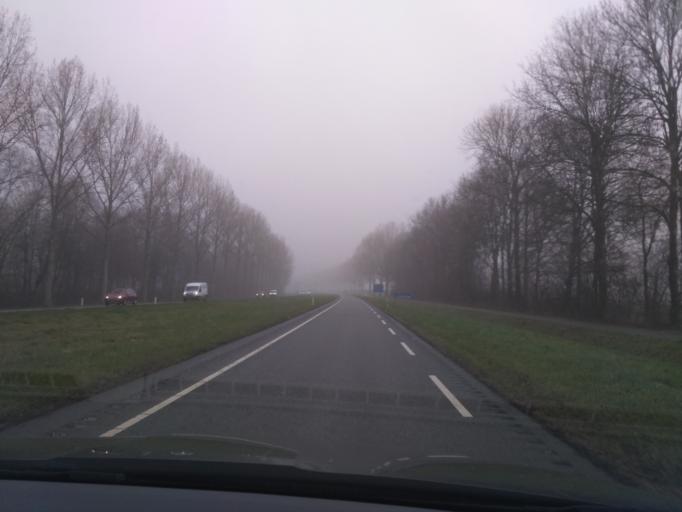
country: NL
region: Flevoland
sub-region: Gemeente Dronten
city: Dronten
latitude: 52.5110
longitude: 5.7300
